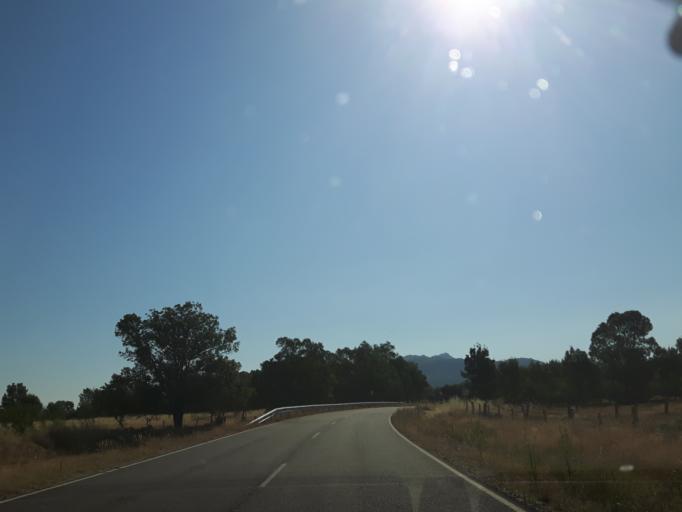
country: ES
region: Castille and Leon
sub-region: Provincia de Salamanca
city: Valdehijaderos
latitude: 40.4208
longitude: -5.8384
